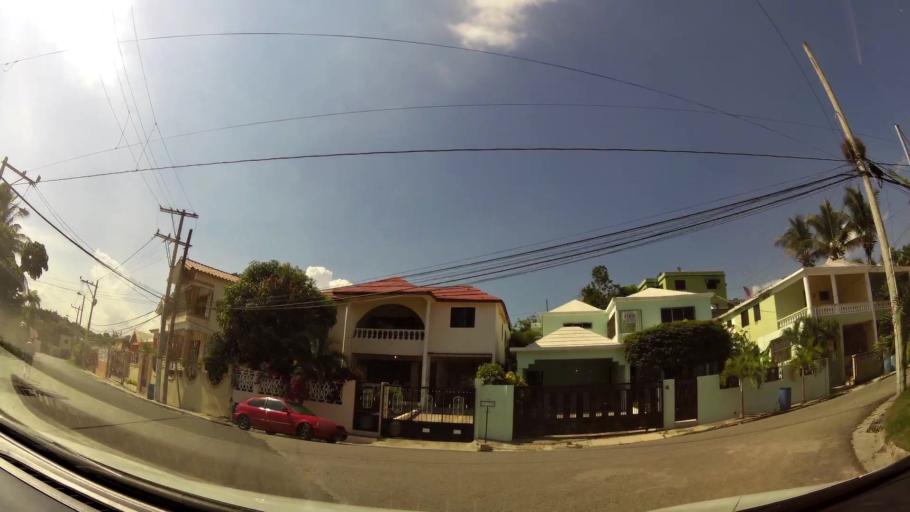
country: DO
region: Santo Domingo
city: Santo Domingo Oeste
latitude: 18.4747
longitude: -70.0043
